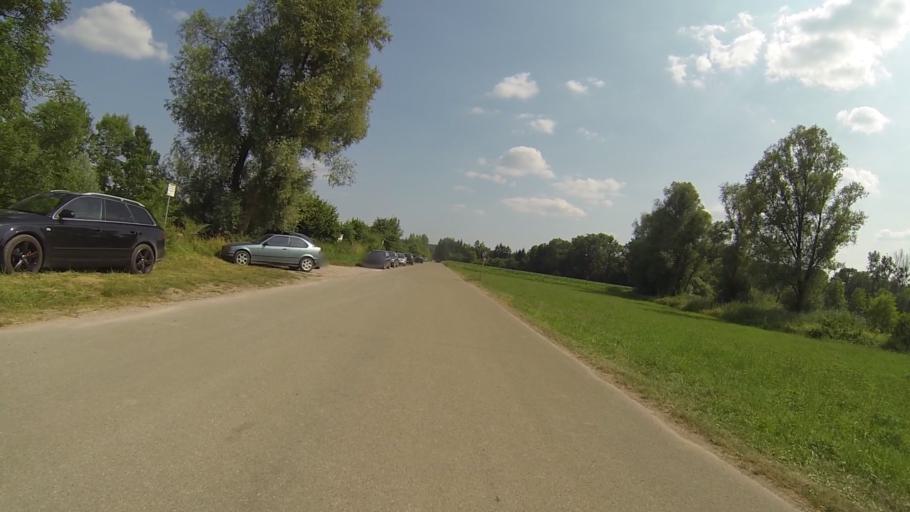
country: DE
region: Bavaria
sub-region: Swabia
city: Guenzburg
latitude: 48.4832
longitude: 10.3047
